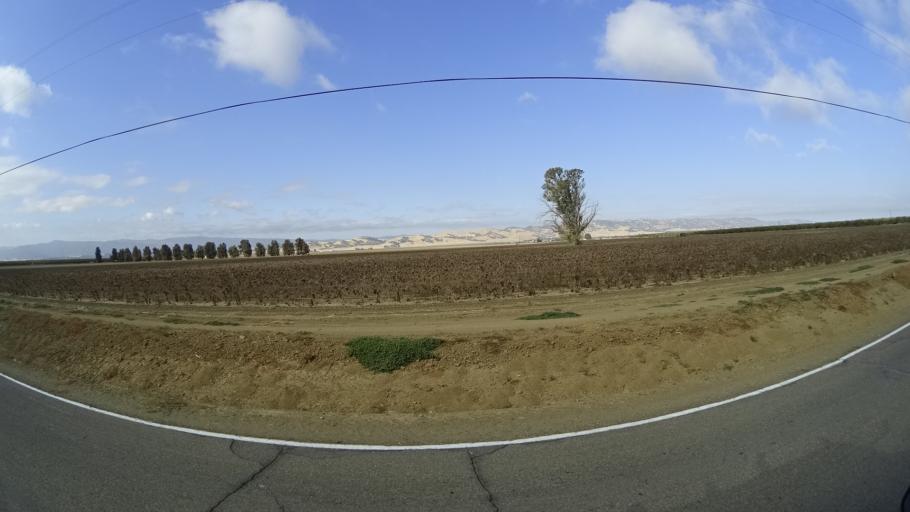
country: US
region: California
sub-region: Yolo County
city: Esparto
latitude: 38.7486
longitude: -122.0072
